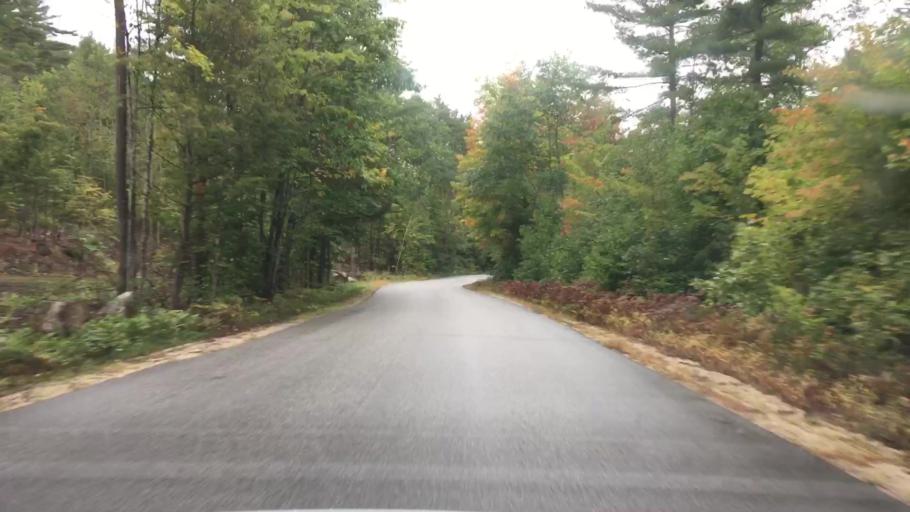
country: US
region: Maine
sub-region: Cumberland County
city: Harrison
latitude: 44.0164
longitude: -70.5850
